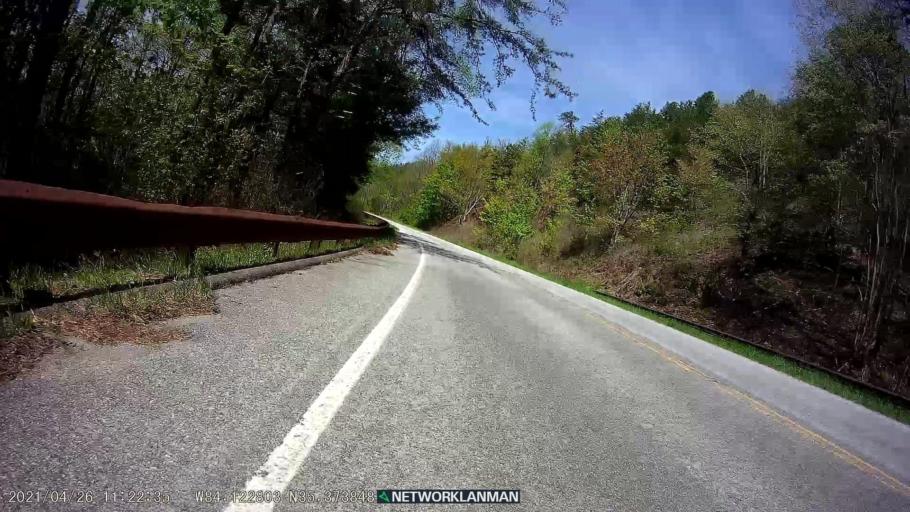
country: US
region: Tennessee
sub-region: Monroe County
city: Vonore
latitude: 35.3737
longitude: -84.1228
